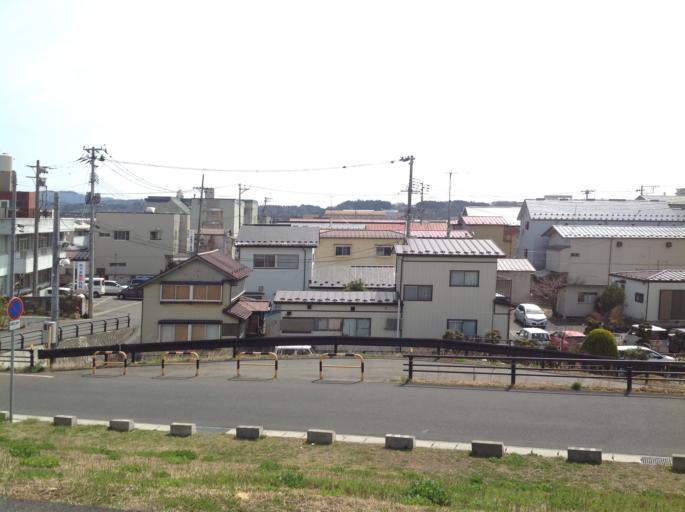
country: JP
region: Iwate
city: Ichinoseki
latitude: 38.9331
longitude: 141.1329
